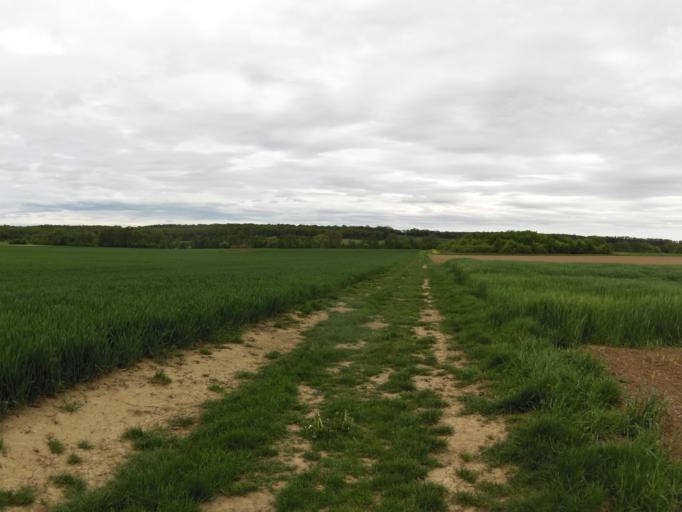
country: DE
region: Bavaria
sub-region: Regierungsbezirk Unterfranken
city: Unterpleichfeld
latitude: 49.8506
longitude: 10.0552
